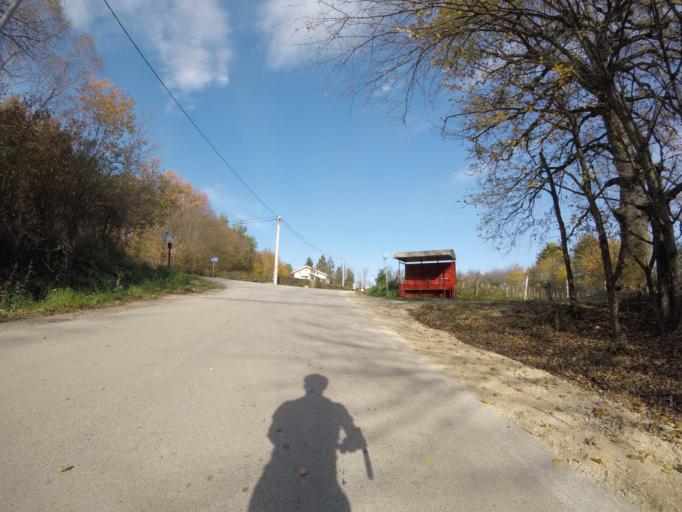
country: HR
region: Zagrebacka
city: Gradici
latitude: 45.6322
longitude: 16.0227
